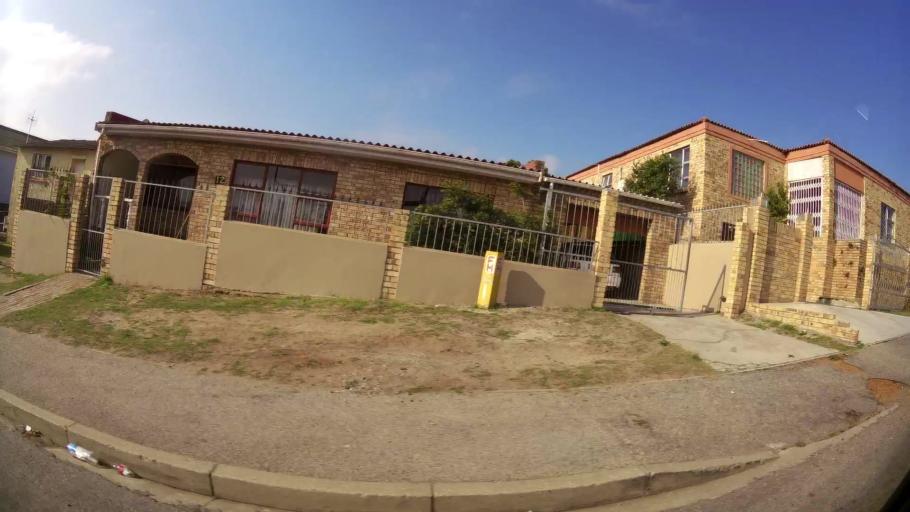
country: ZA
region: Eastern Cape
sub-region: Nelson Mandela Bay Metropolitan Municipality
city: Port Elizabeth
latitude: -33.9228
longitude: 25.5582
